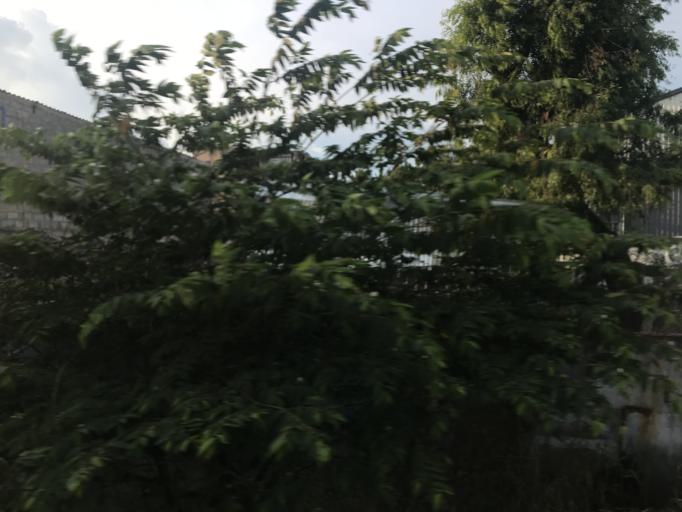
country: IN
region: Tamil Nadu
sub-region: Coimbatore
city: Coimbatore
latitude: 11.0303
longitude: 76.9825
